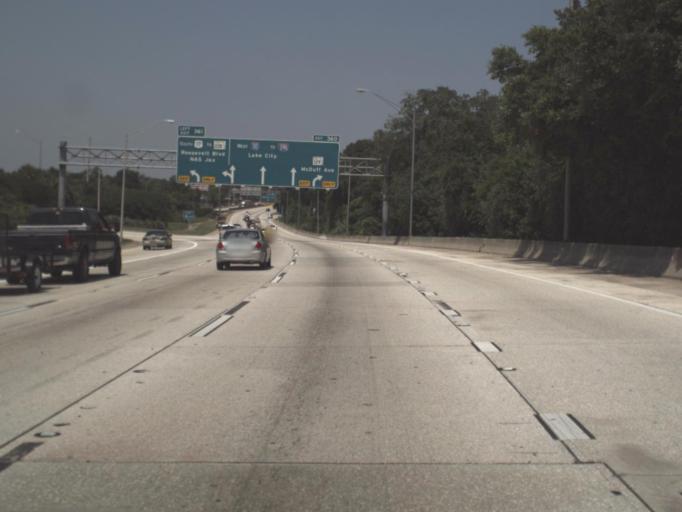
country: US
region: Florida
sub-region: Duval County
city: Jacksonville
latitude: 30.3219
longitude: -81.6975
